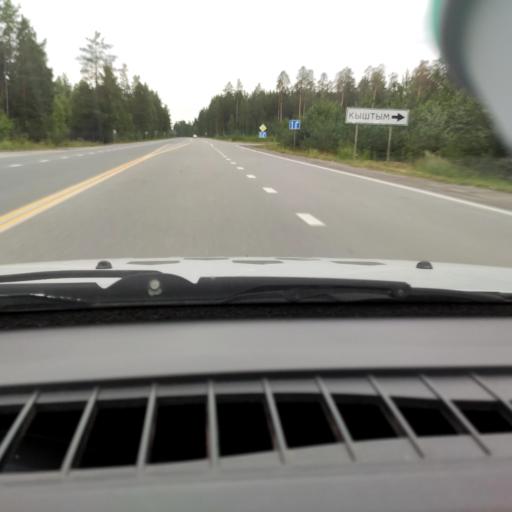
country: RU
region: Chelyabinsk
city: Kyshtym
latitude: 55.6929
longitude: 60.5005
